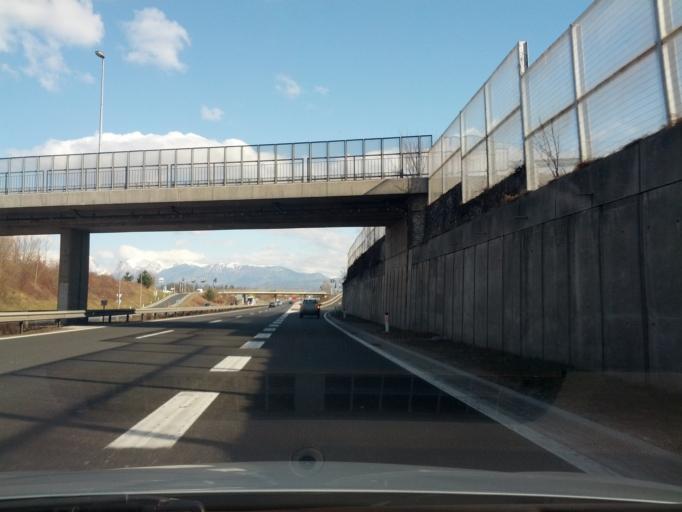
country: SI
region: Dol pri Ljubljani
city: Dol pri Ljubljani
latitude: 46.0883
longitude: 14.5857
